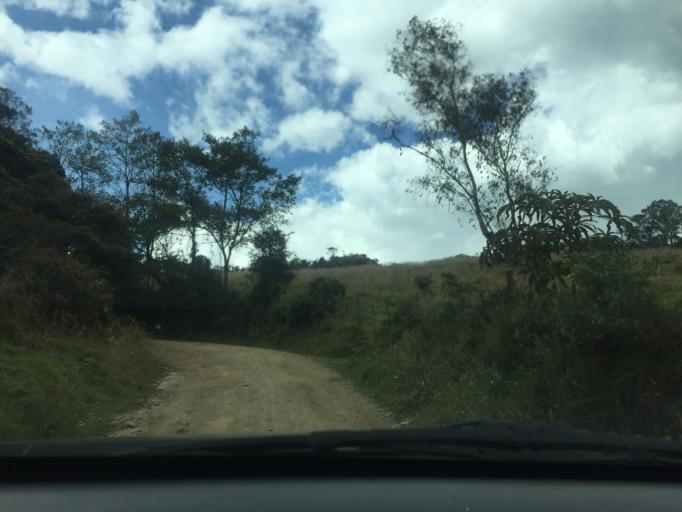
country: CO
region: Cundinamarca
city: Facatativa
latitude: 4.7997
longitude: -74.3827
